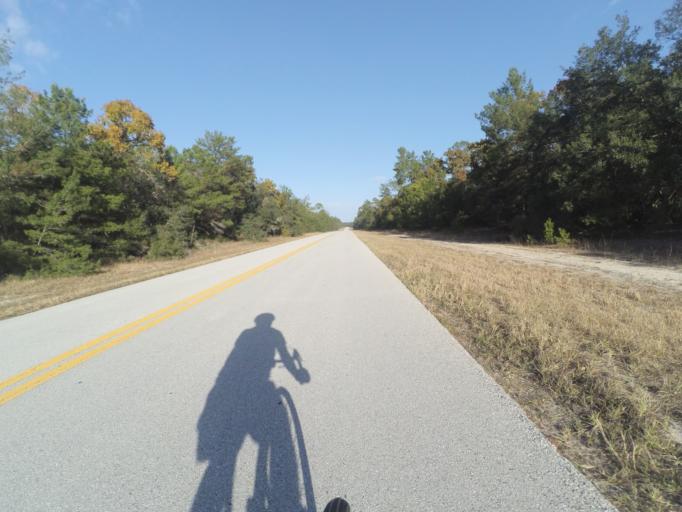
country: US
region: Florida
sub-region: Lake County
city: Astor
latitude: 29.1014
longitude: -81.5658
